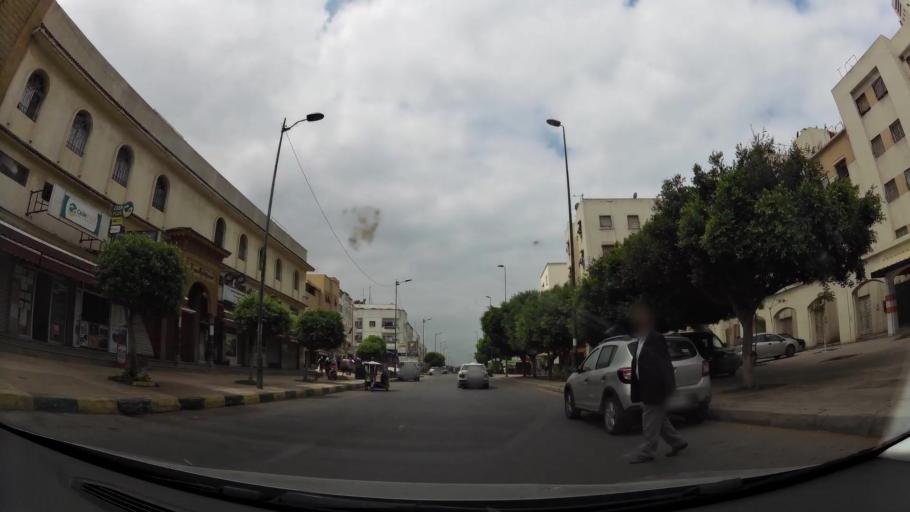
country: MA
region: Rabat-Sale-Zemmour-Zaer
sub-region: Rabat
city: Rabat
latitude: 33.9981
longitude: -6.8741
